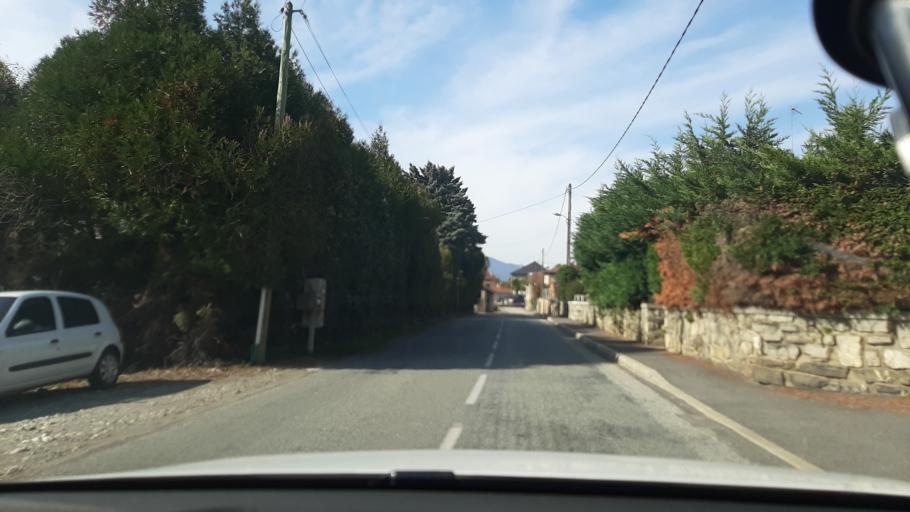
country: FR
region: Rhone-Alpes
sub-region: Departement de la Savoie
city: La Rochette
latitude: 45.4466
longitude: 6.0737
